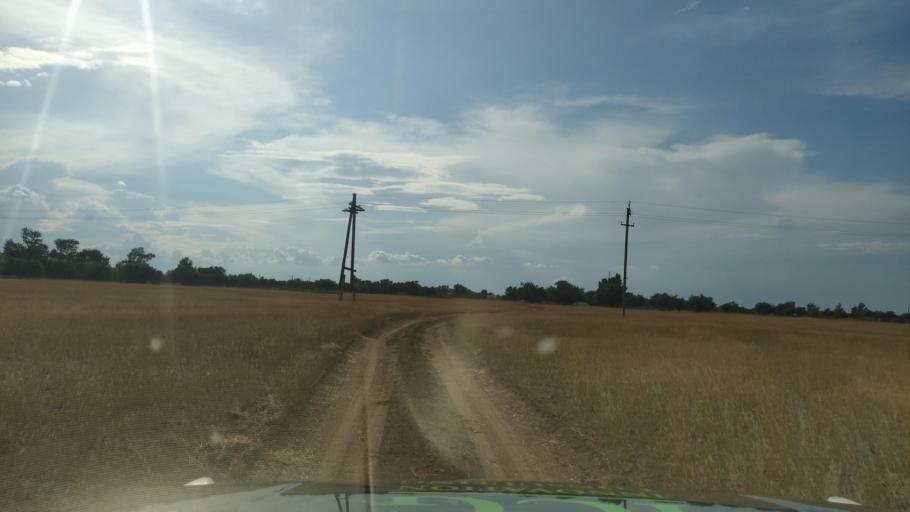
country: KZ
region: Pavlodar
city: Pavlodar
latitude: 52.5152
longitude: 77.4480
